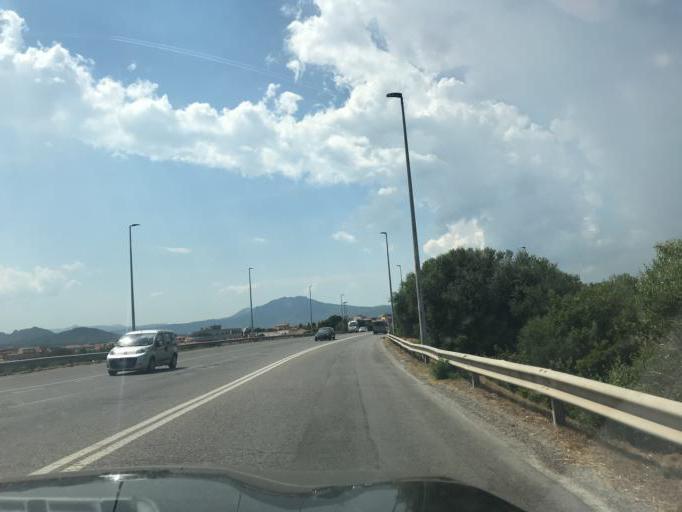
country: IT
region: Sardinia
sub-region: Provincia di Olbia-Tempio
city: Olbia
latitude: 40.9104
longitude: 9.5055
